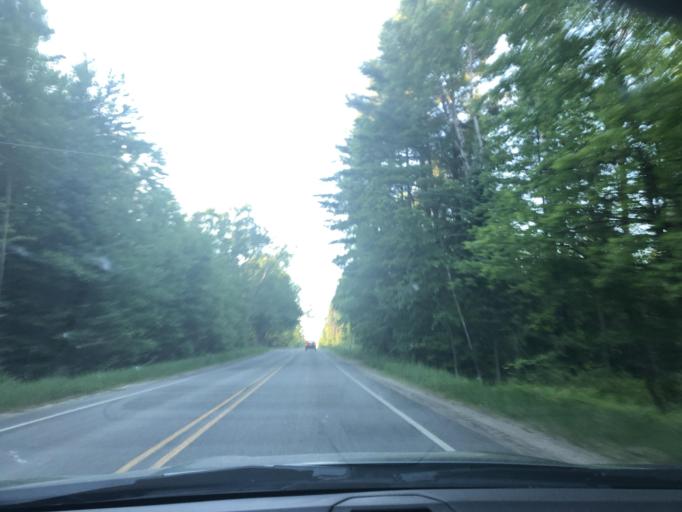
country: US
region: Michigan
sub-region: Missaukee County
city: Lake City
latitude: 44.4434
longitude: -85.0749
